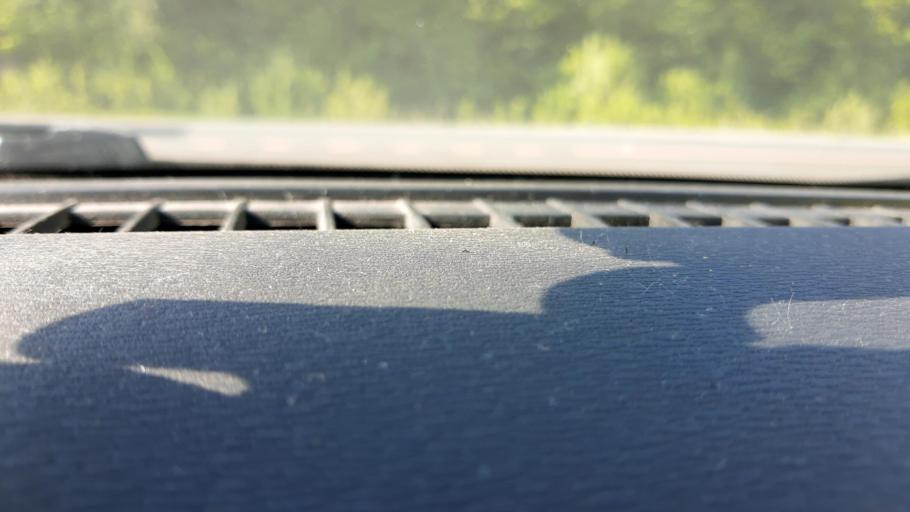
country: RU
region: Bashkortostan
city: Iglino
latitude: 54.7651
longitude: 56.4201
